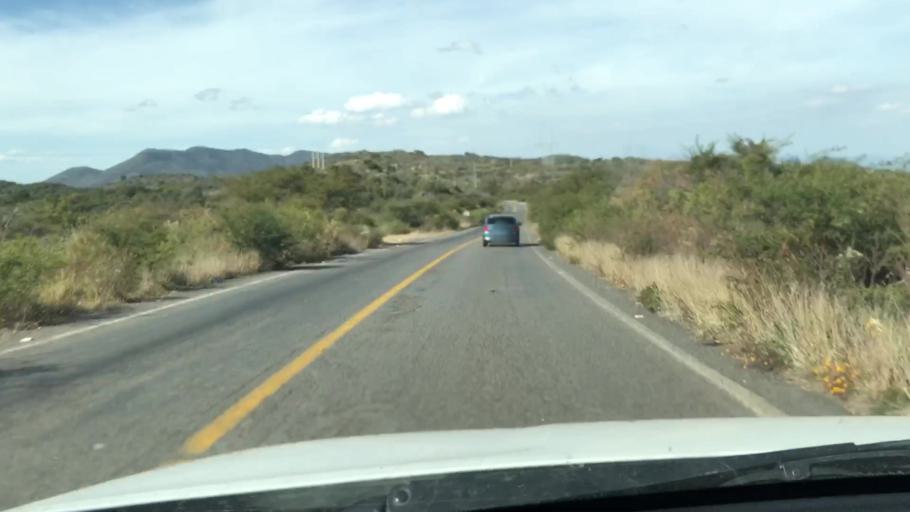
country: MX
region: Jalisco
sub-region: Zacoalco de Torres
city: Barranca de Otates (Barranca de Otatan)
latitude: 20.2058
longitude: -103.6918
